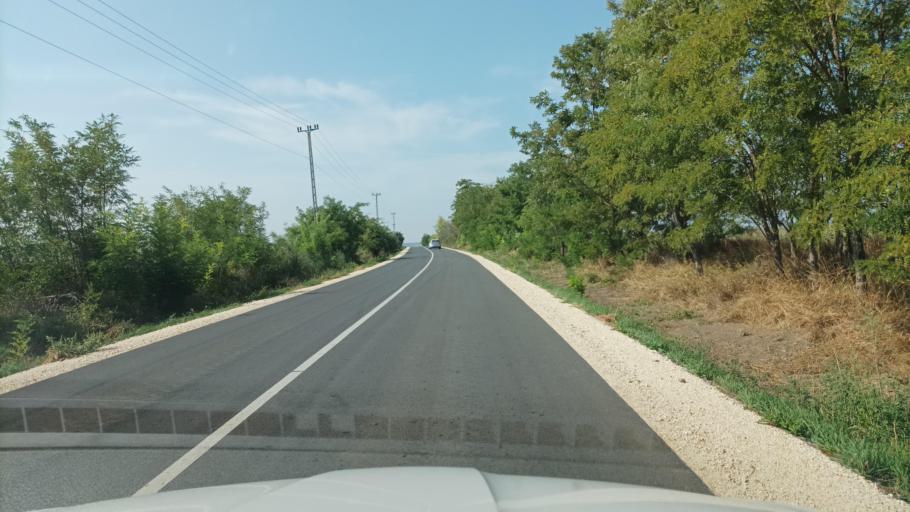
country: HU
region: Pest
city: Vacszentlaszlo
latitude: 47.5790
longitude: 19.5523
